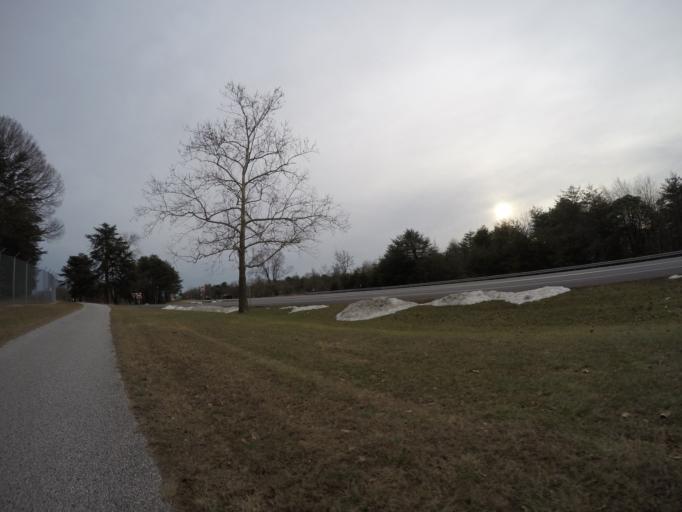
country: US
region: Maryland
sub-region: Anne Arundel County
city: Severn
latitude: 39.1621
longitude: -76.6953
